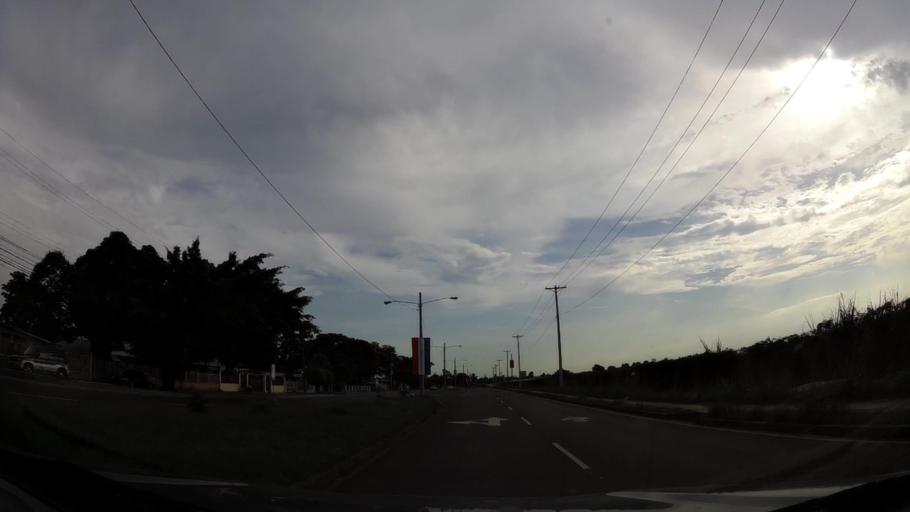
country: PA
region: Panama
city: Tocumen
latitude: 9.0832
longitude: -79.3668
